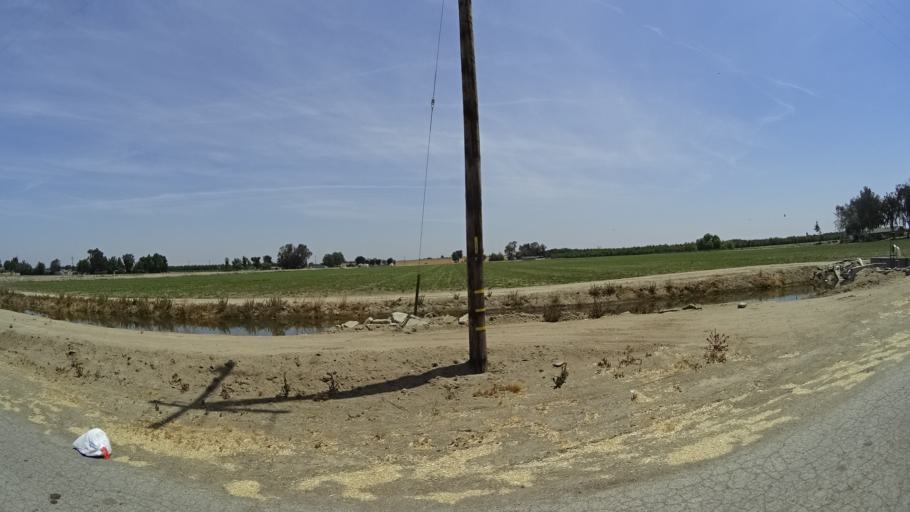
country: US
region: California
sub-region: Fresno County
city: Riverdale
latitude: 36.3997
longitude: -119.8163
